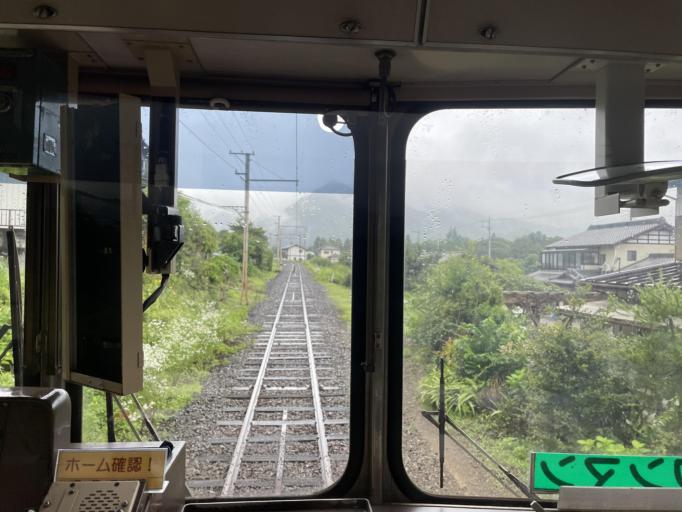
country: JP
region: Saitama
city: Chichibu
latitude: 35.9590
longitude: 138.9903
